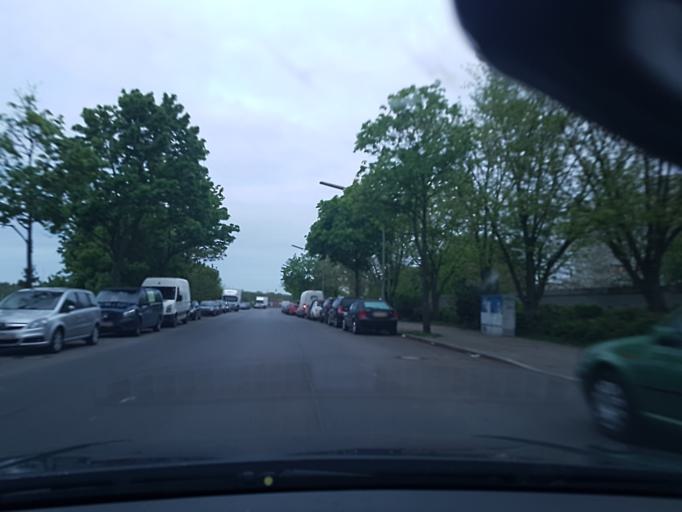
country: DE
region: Berlin
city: Britz
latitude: 52.4168
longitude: 13.4354
